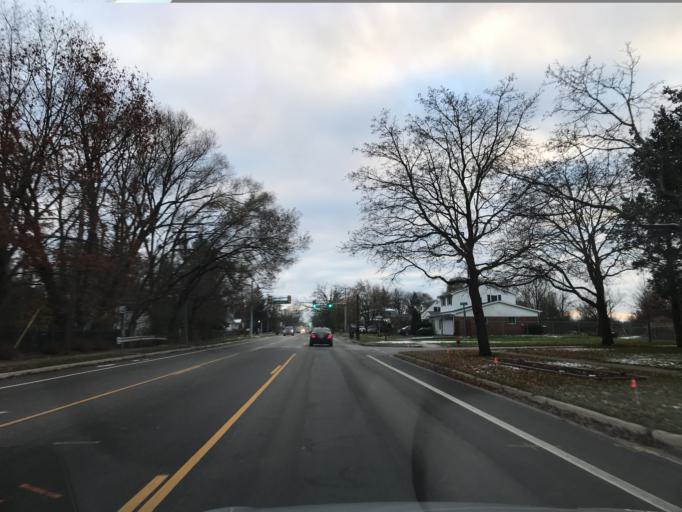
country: US
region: Michigan
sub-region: Washtenaw County
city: Ann Arbor
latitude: 42.2393
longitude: -83.7001
